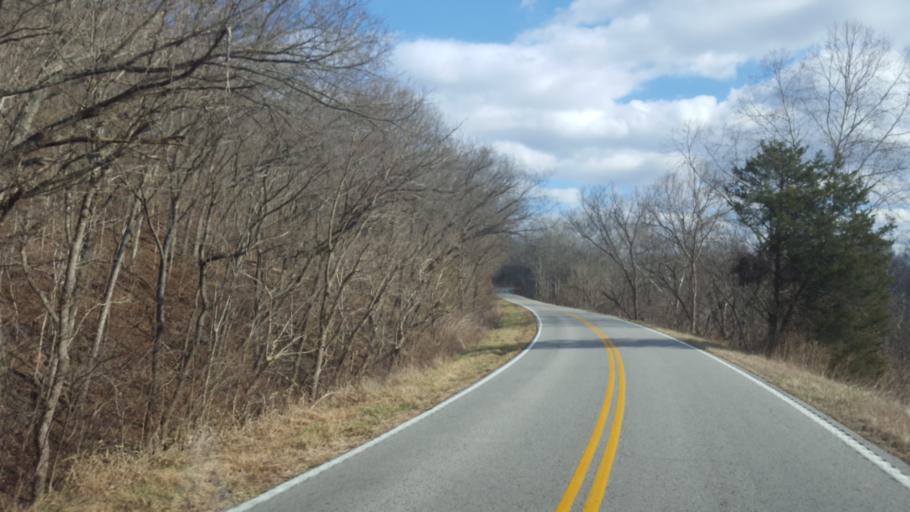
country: US
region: Kentucky
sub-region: Owen County
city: Owenton
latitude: 38.4470
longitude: -84.9084
